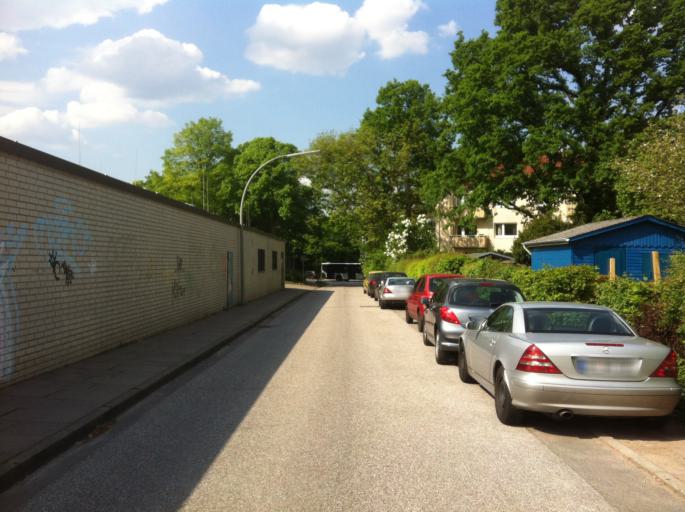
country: DE
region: Hamburg
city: Altona
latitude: 53.5546
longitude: 9.9050
